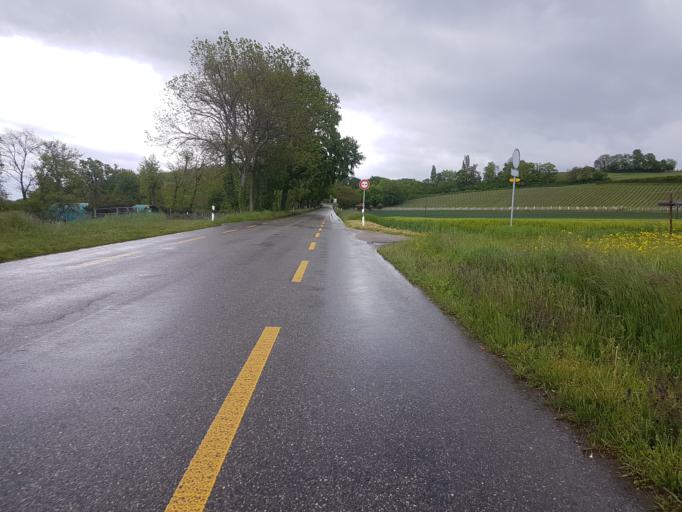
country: CH
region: Geneva
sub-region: Geneva
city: Dardagny
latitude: 46.1747
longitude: 5.9999
